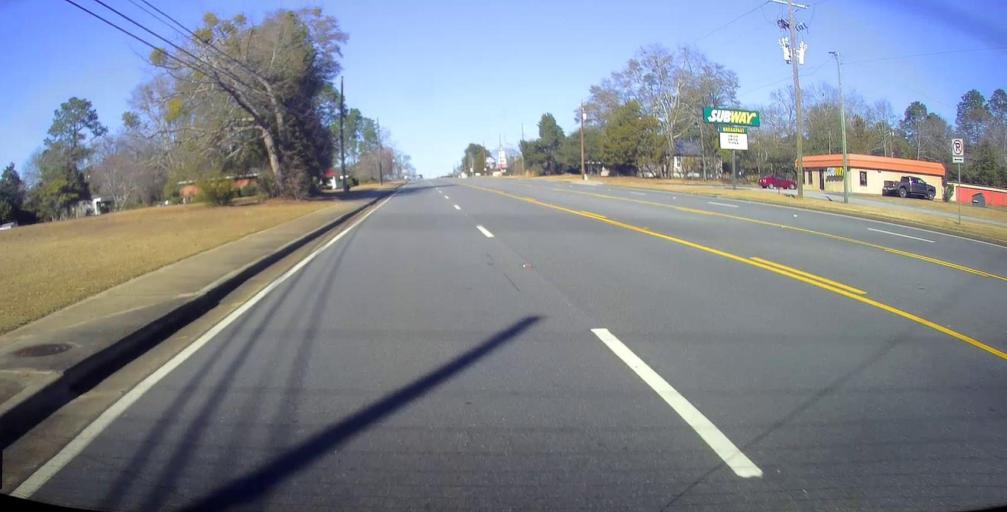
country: US
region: Georgia
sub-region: Taylor County
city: Butler
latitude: 32.5518
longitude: -84.2401
